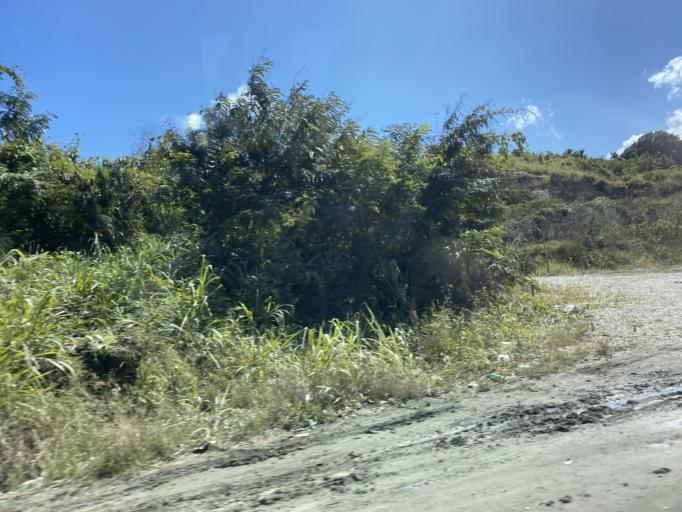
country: DO
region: Puerto Plata
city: Imbert
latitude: 19.8204
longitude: -70.7771
